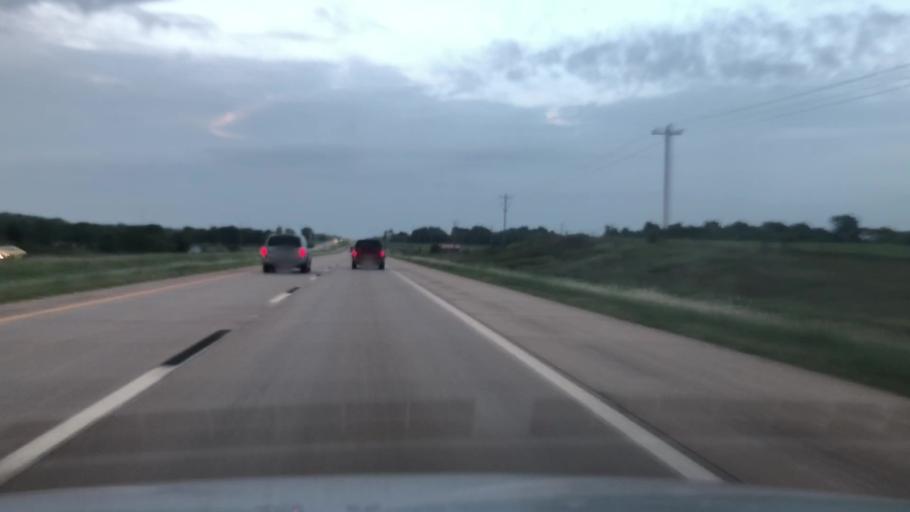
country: US
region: Oklahoma
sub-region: Osage County
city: Skiatook
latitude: 36.4491
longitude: -95.9204
